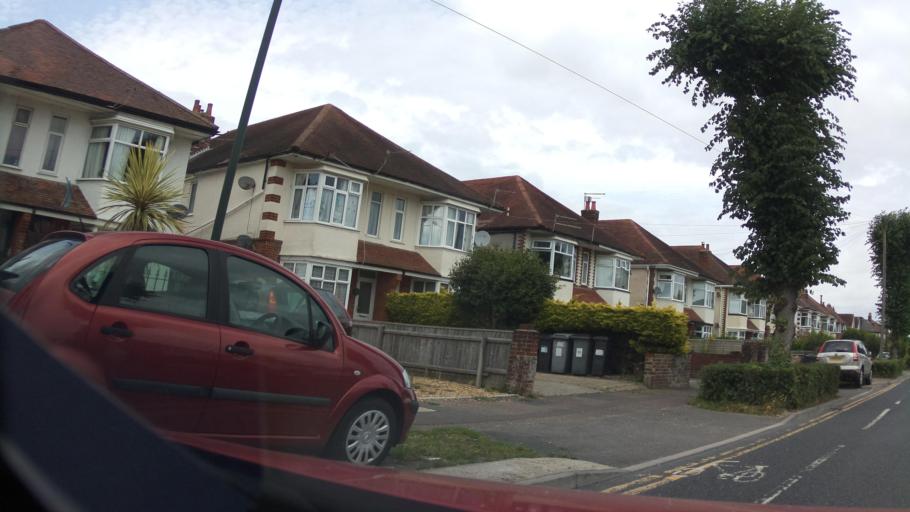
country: GB
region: England
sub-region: Dorset
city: Christchurch
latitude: 50.7374
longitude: -1.8125
